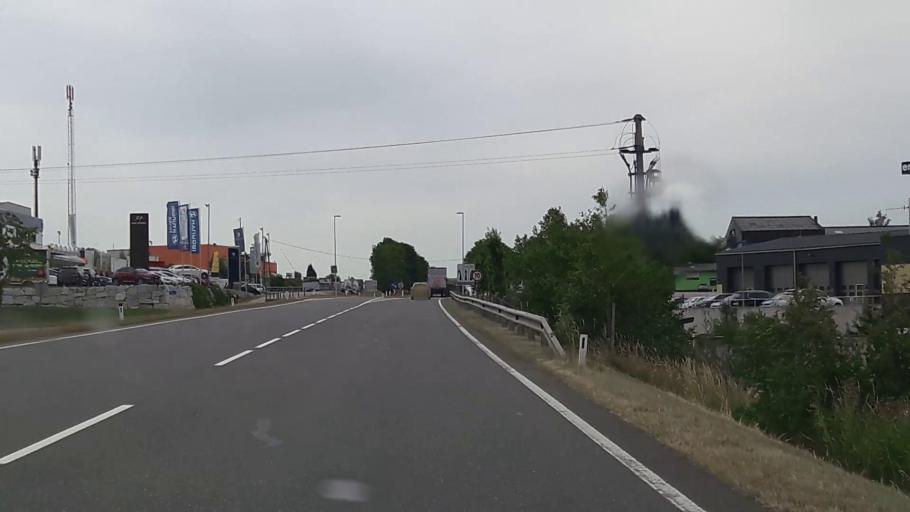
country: AT
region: Upper Austria
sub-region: Politischer Bezirk Urfahr-Umgebung
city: Herzogsdorf
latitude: 48.4191
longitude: 14.0597
